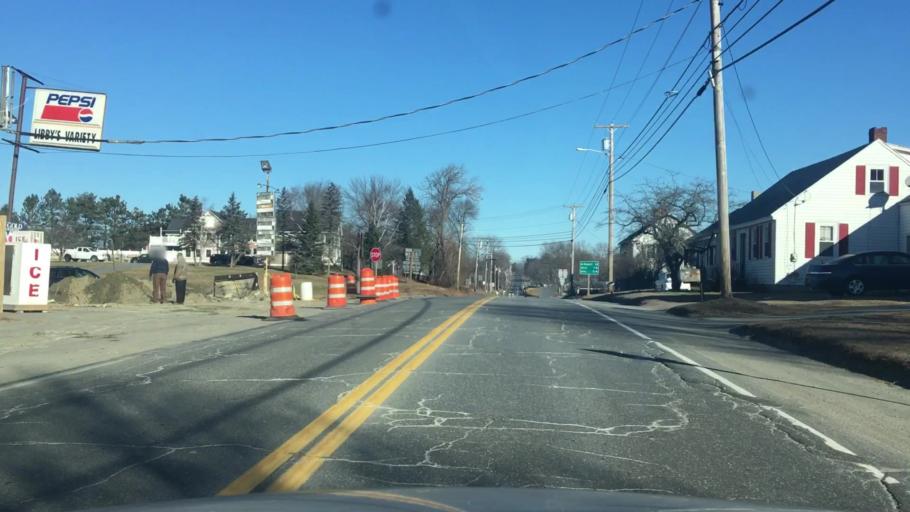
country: US
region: Maine
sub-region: Kennebec County
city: Benton
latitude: 44.5847
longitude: -69.5523
